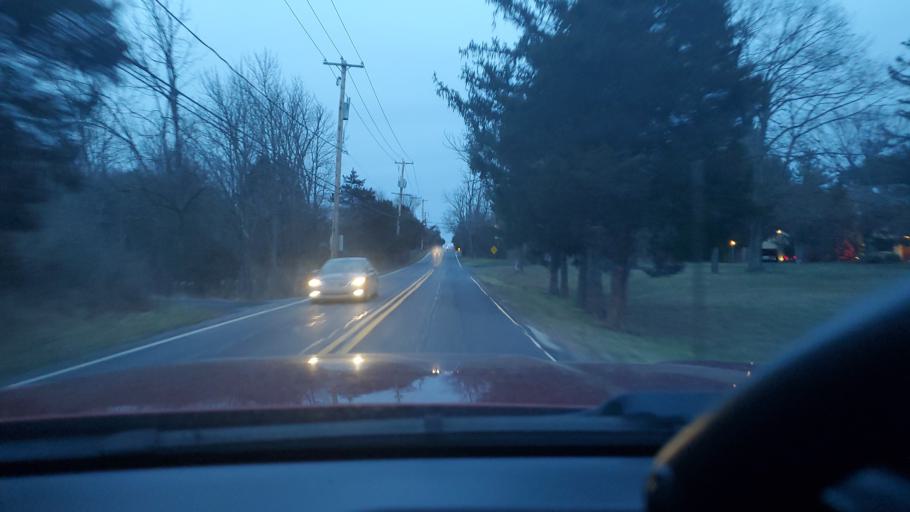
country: US
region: Pennsylvania
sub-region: Montgomery County
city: Trappe
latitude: 40.2279
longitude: -75.4868
